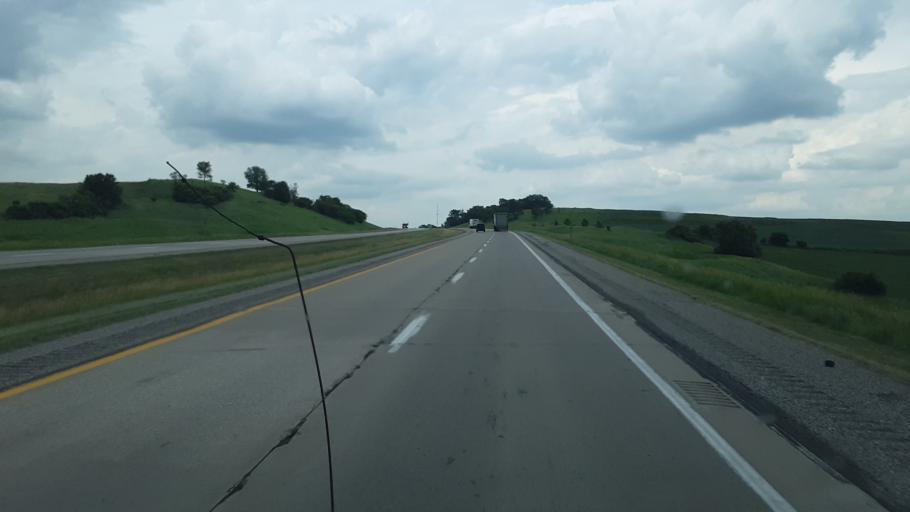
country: US
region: Iowa
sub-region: Pottawattamie County
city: Avoca
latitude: 41.4756
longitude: -95.5901
